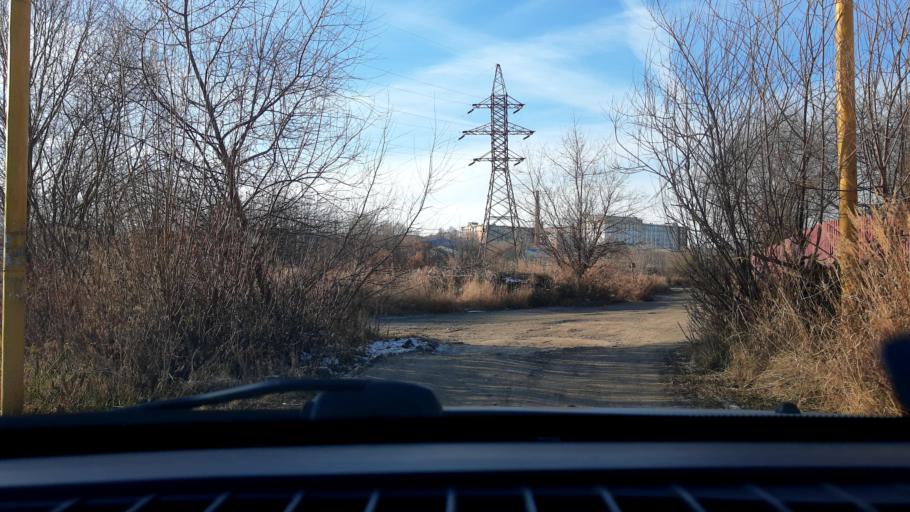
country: RU
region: Nizjnij Novgorod
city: Nizhniy Novgorod
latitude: 56.2487
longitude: 43.9986
